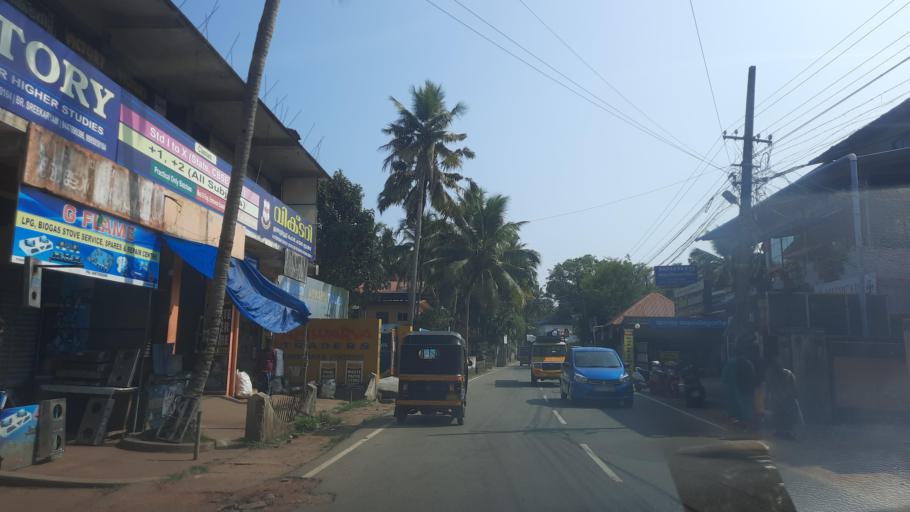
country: IN
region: Kerala
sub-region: Thiruvananthapuram
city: Nedumangad
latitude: 8.5762
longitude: 76.9254
